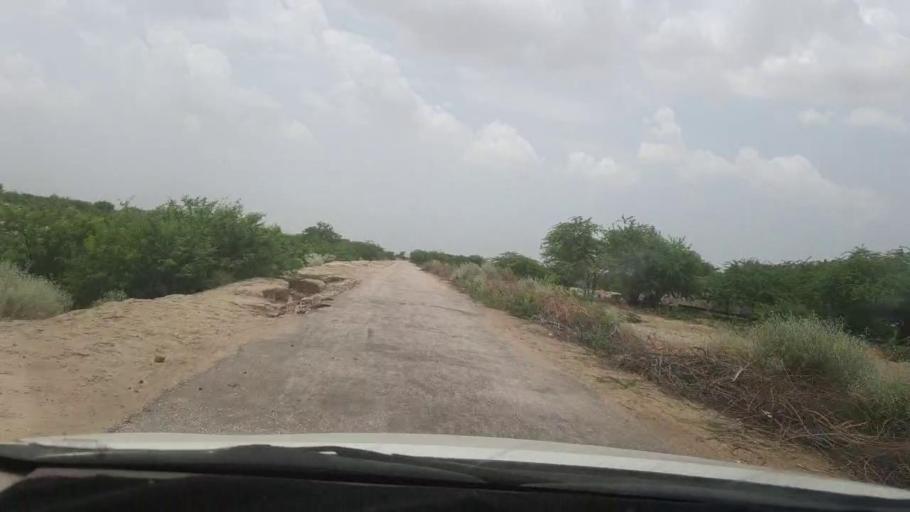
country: PK
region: Sindh
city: Khairpur
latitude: 27.3958
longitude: 68.9835
